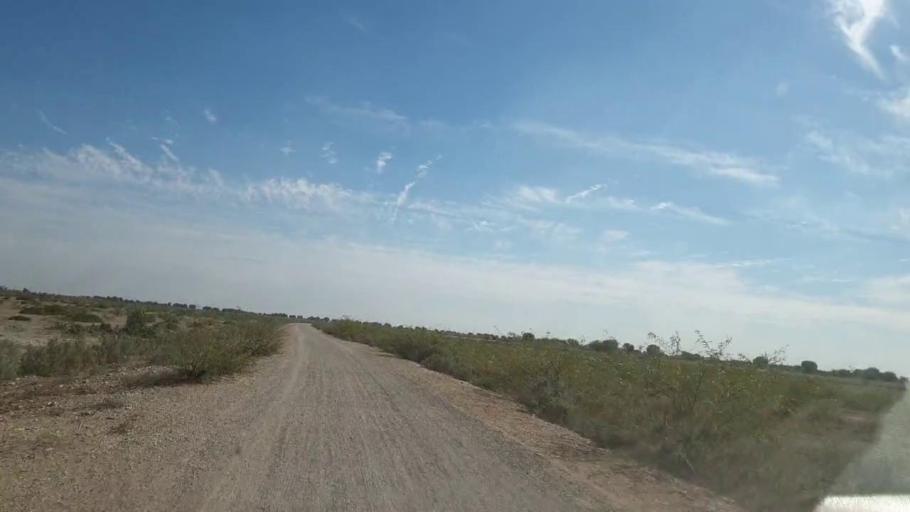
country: PK
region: Sindh
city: Pithoro
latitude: 25.5609
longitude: 69.3025
